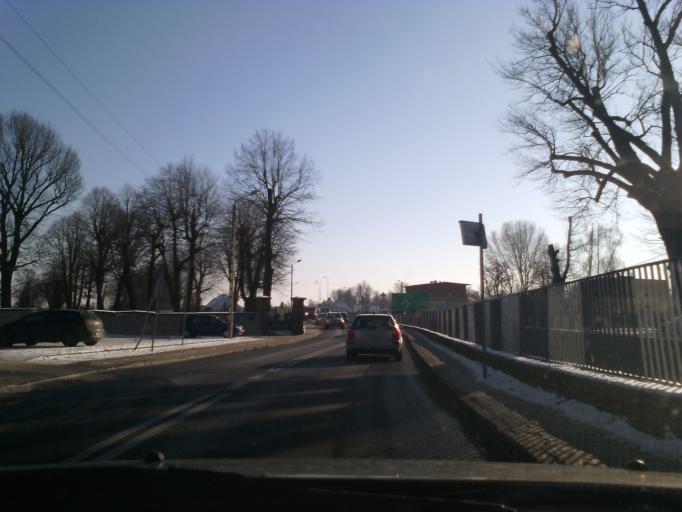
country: PL
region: Lower Silesian Voivodeship
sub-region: Powiat swidnicki
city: Strzegom
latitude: 50.9562
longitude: 16.3499
